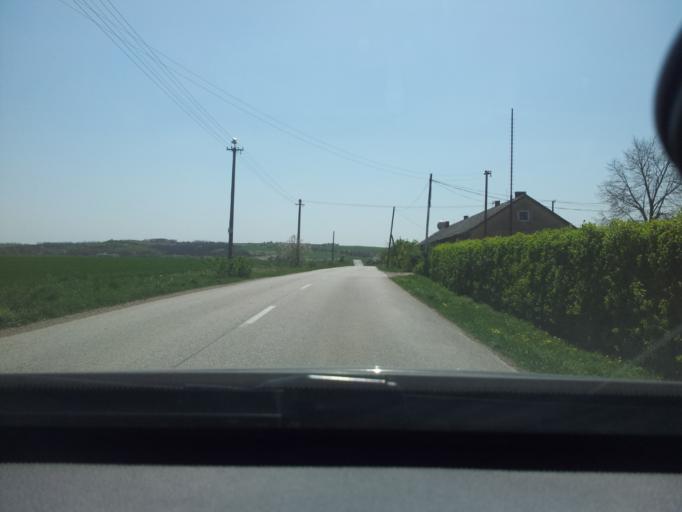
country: SK
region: Nitriansky
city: Zlate Moravce
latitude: 48.3483
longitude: 18.4220
